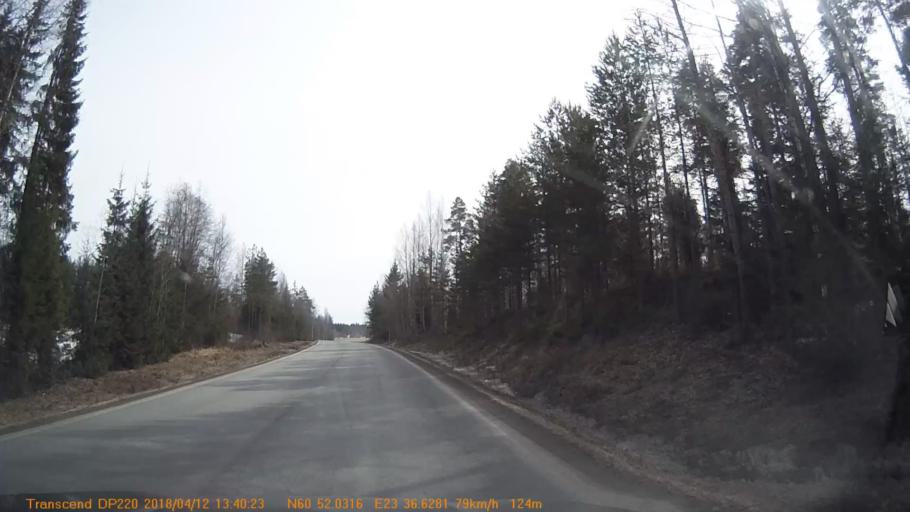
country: FI
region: Haeme
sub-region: Forssa
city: Forssa
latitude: 60.8665
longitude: 23.6111
